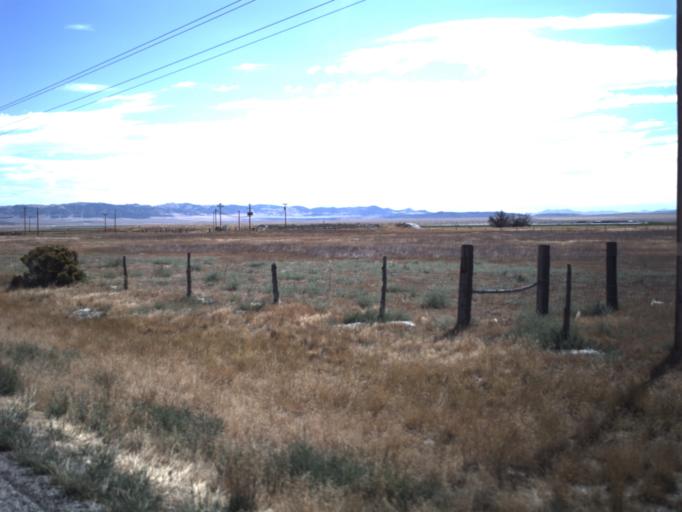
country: US
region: Idaho
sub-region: Oneida County
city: Malad City
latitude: 41.9664
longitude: -112.9249
